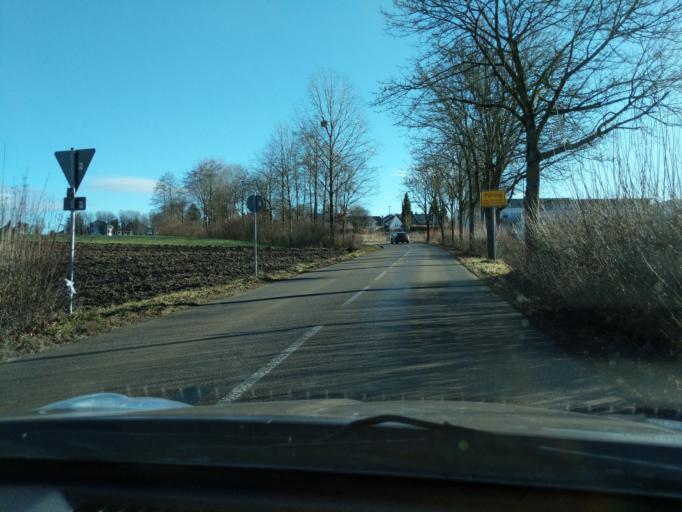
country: DE
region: Bavaria
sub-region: Upper Bavaria
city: Zorneding
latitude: 48.0944
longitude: 11.8238
